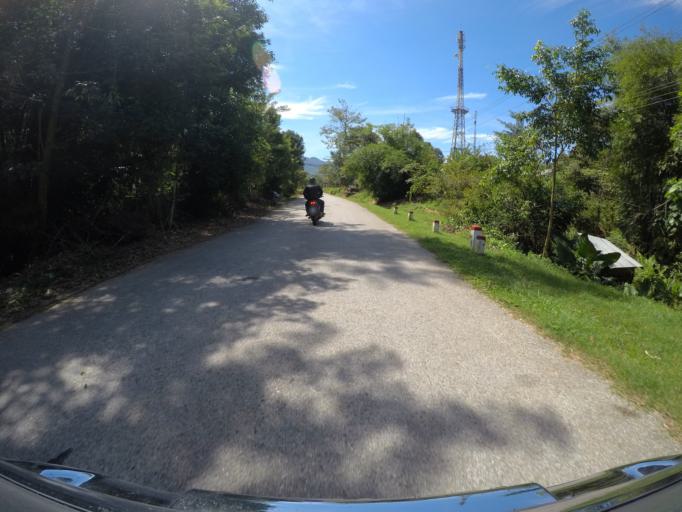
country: VN
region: Quang Nam
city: Thanh My
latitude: 15.6620
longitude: 107.7035
